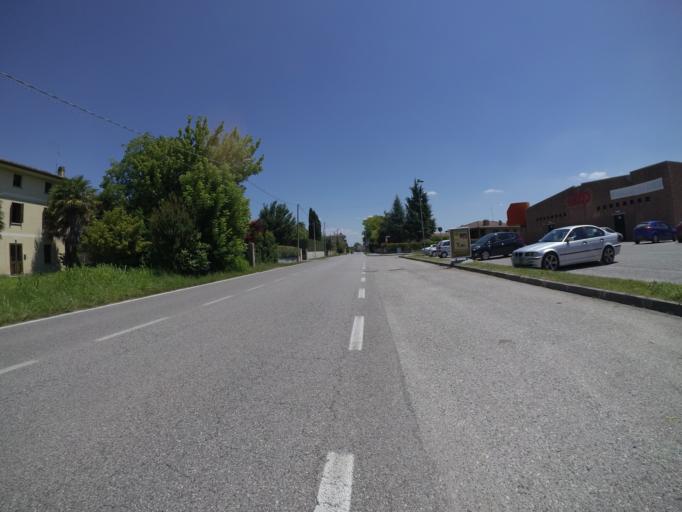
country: IT
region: Friuli Venezia Giulia
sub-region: Provincia di Udine
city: Rivignano
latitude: 45.8785
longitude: 13.0360
